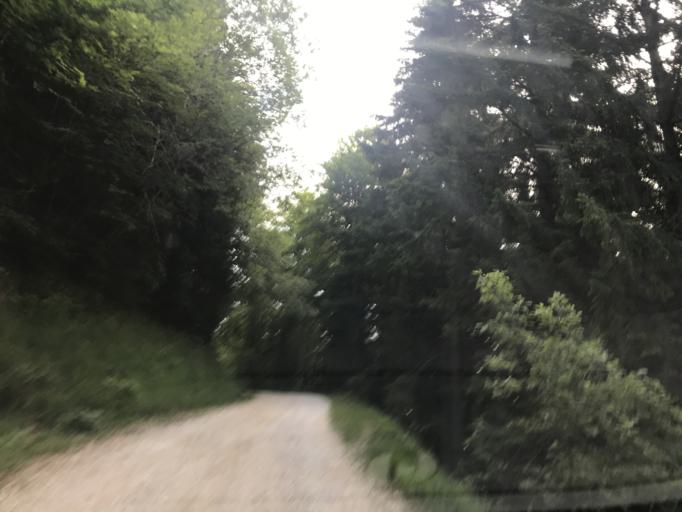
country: FR
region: Rhone-Alpes
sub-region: Departement de l'Isere
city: Saint-Vincent-de-Mercuze
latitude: 45.4146
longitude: 5.9367
